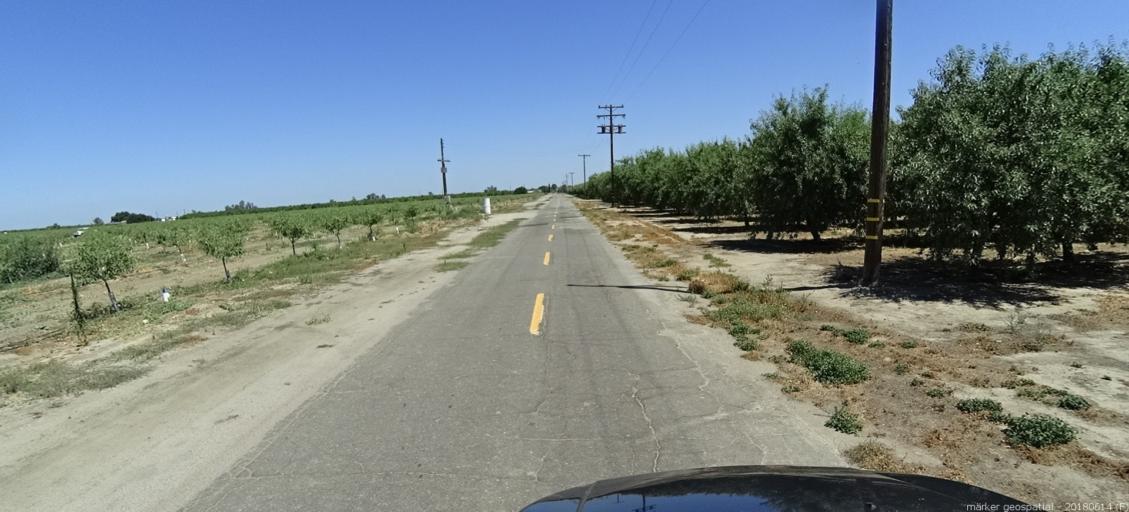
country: US
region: California
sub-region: Madera County
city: Fairmead
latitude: 36.9917
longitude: -120.2476
